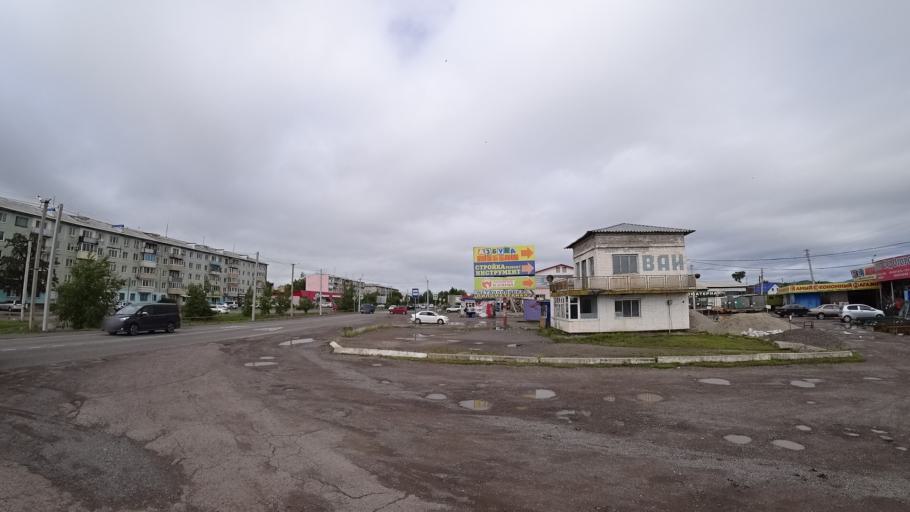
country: RU
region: Primorskiy
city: Monastyrishche
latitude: 44.2041
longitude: 132.4505
